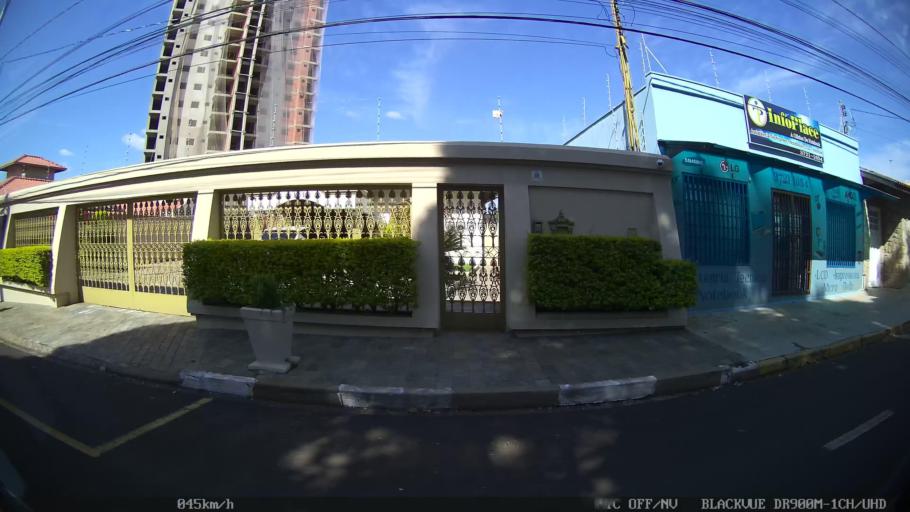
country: BR
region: Sao Paulo
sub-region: Franca
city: Franca
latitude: -20.5368
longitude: -47.4115
